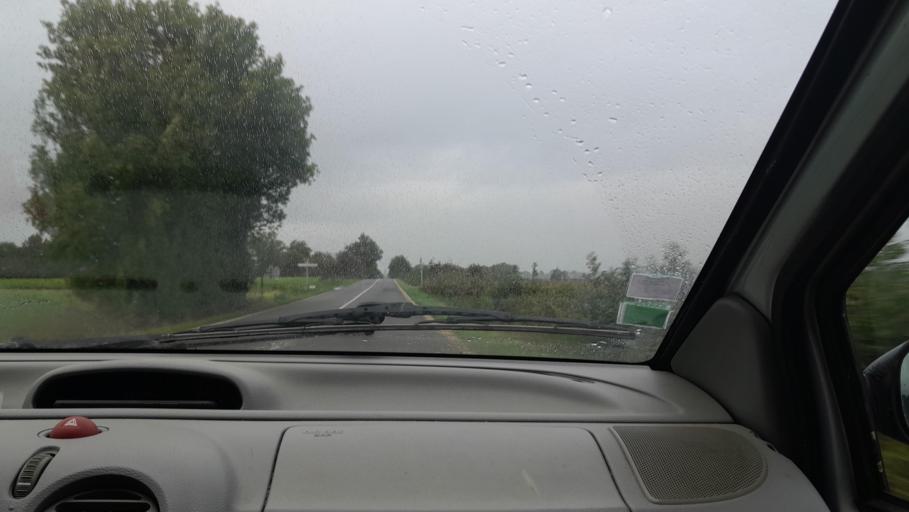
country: FR
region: Pays de la Loire
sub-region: Departement de la Mayenne
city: Congrier
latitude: 47.8249
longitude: -1.1435
